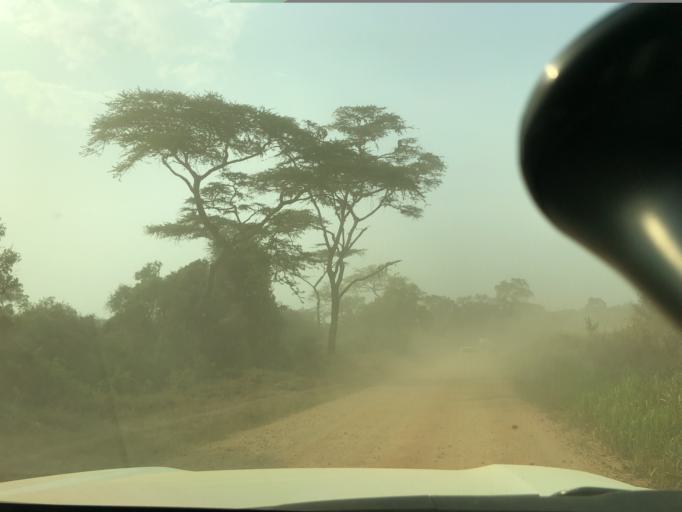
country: CD
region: Nord Kivu
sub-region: North Kivu
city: Butembo
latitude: 0.0921
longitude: 29.6407
